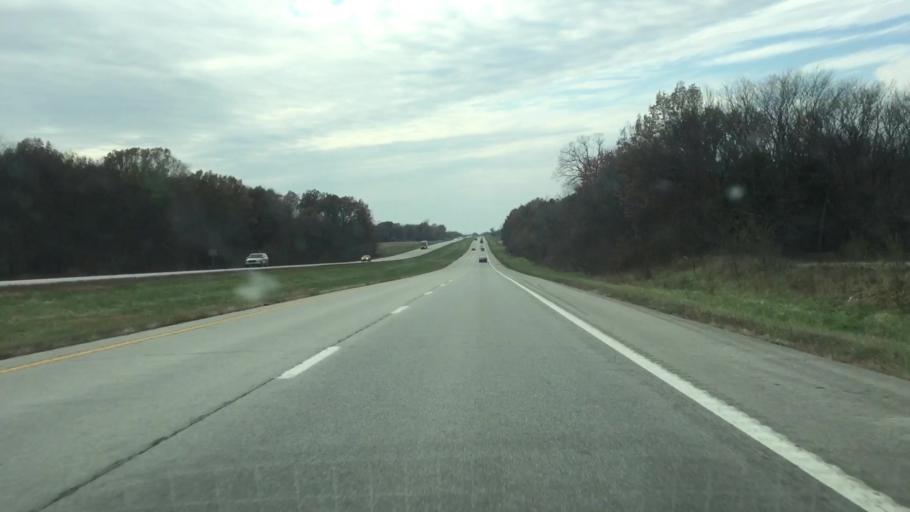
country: US
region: Missouri
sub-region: Cass County
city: Garden City
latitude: 38.6020
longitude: -94.2671
